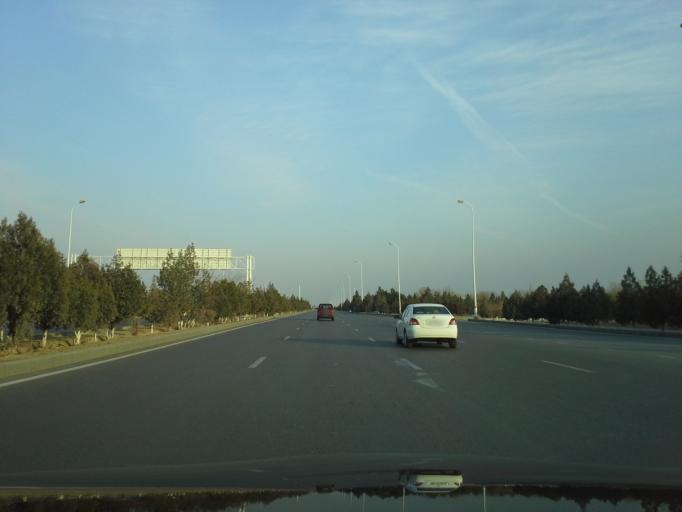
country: TM
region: Ahal
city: Abadan
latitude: 38.0512
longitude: 58.1859
